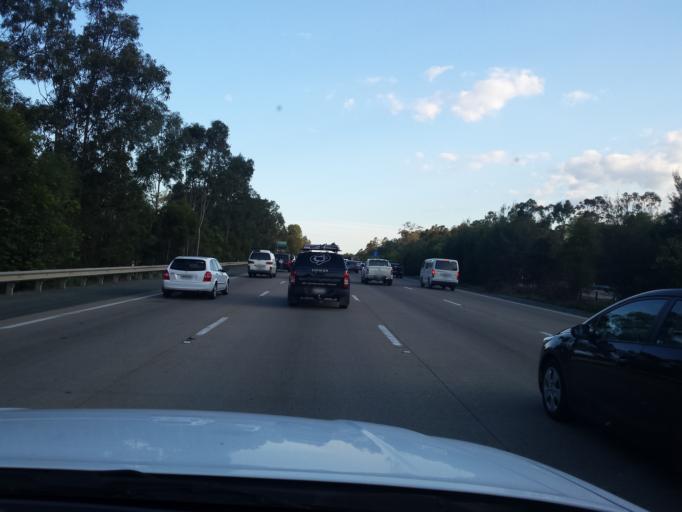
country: AU
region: Queensland
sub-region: Gold Coast
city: Oxenford
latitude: -27.8356
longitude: 153.3027
